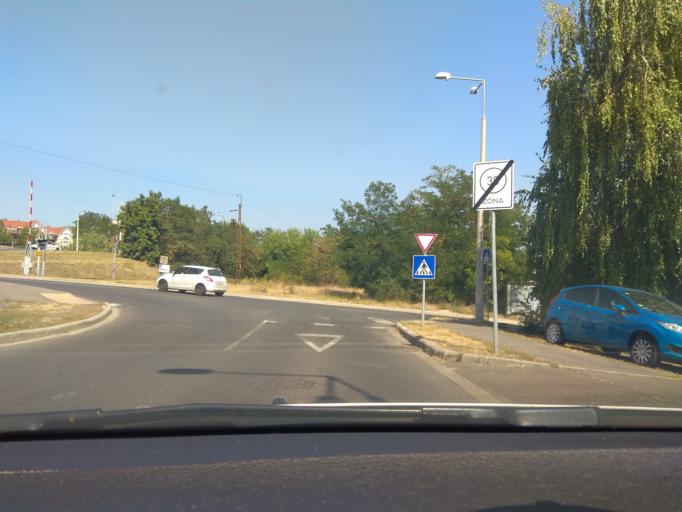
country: HU
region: Borsod-Abauj-Zemplen
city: Miskolc
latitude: 48.0738
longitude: 20.7800
